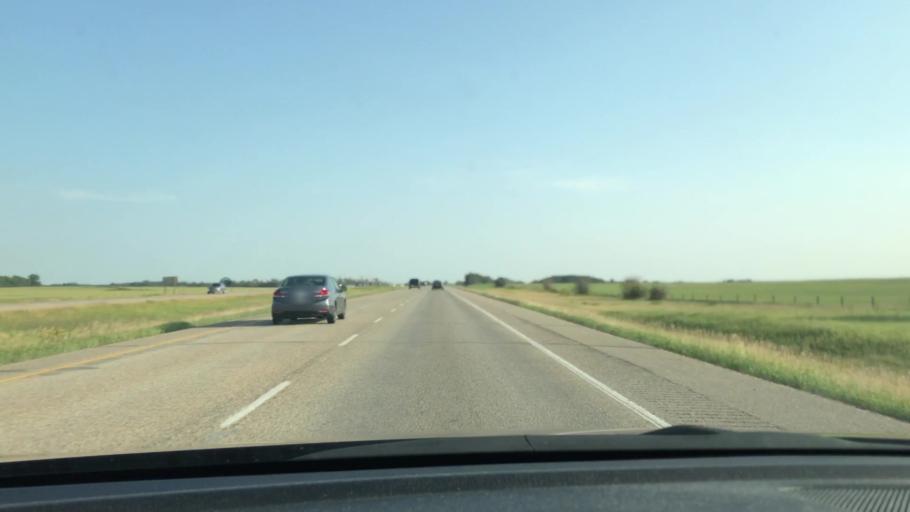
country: CA
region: Alberta
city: Millet
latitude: 53.1097
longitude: -113.5984
